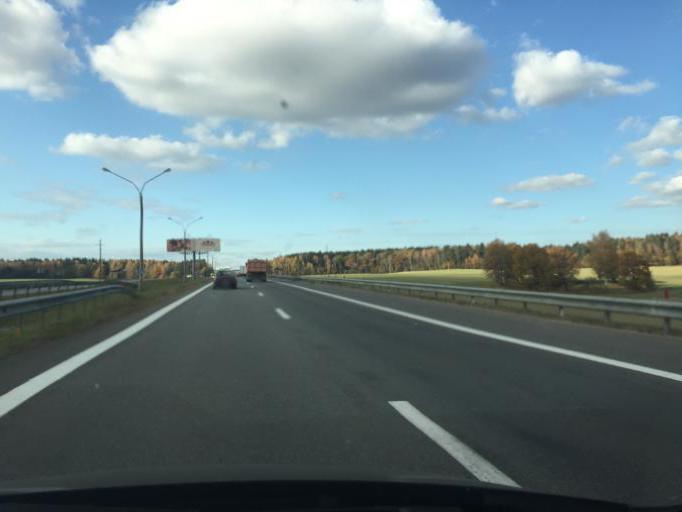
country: BY
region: Minsk
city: Slabada
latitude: 53.9614
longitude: 27.9629
